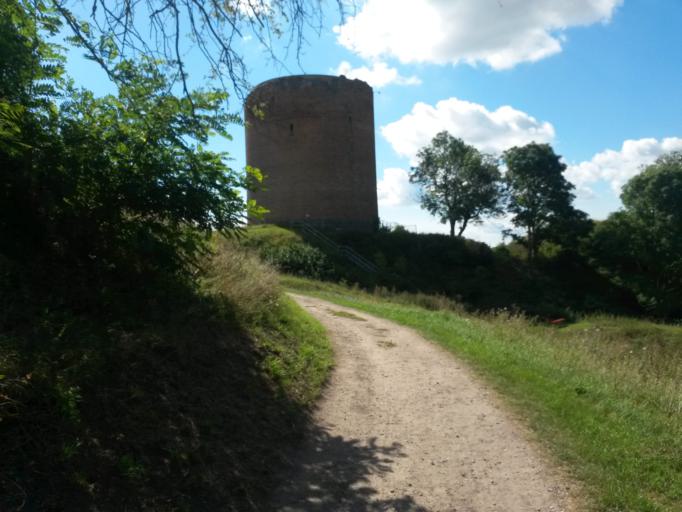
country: DE
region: Brandenburg
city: Schoneberg
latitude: 52.9813
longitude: 14.1155
